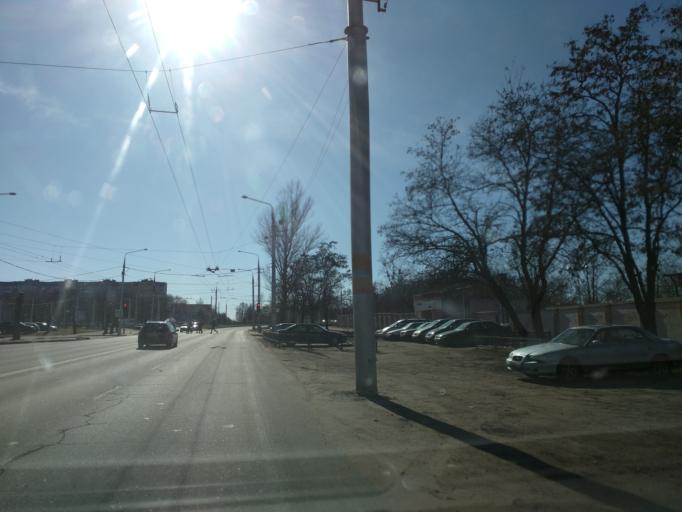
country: BY
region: Mogilev
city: Babruysk
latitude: 53.1789
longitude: 29.2003
